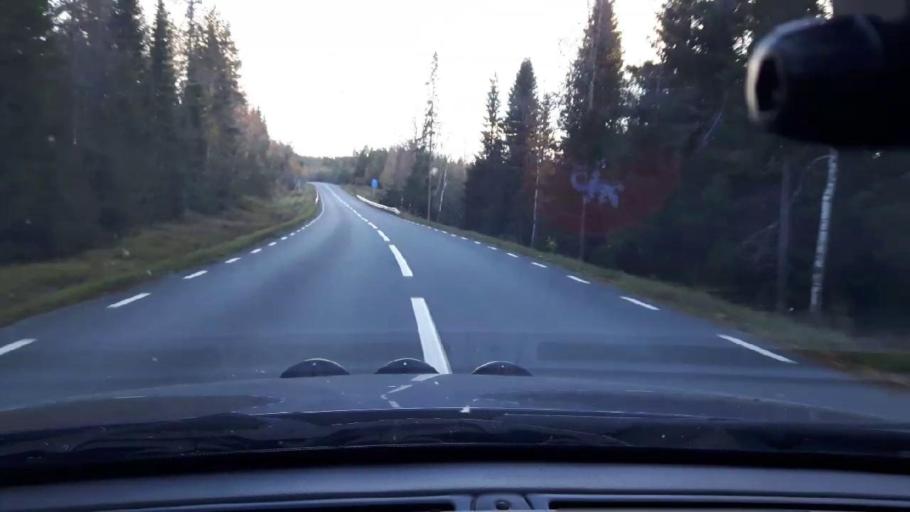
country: SE
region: Jaemtland
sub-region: Bergs Kommun
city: Hoverberg
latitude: 63.0511
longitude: 14.3274
